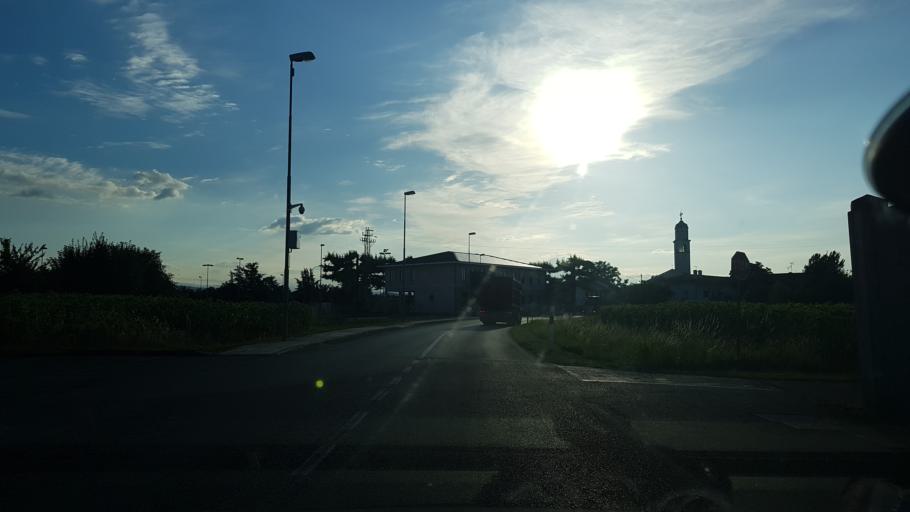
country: IT
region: Friuli Venezia Giulia
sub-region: Provincia di Udine
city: Chiopris
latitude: 45.9241
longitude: 13.3987
